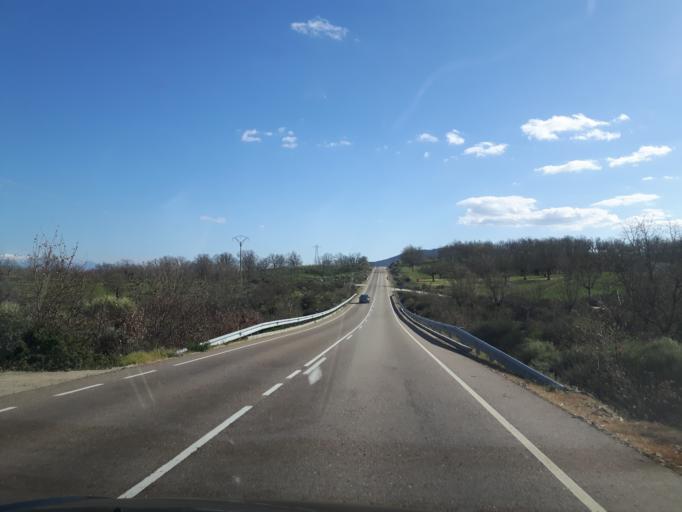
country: ES
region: Castille and Leon
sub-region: Provincia de Salamanca
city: Linares de Riofrio
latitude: 40.6143
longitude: -5.9094
